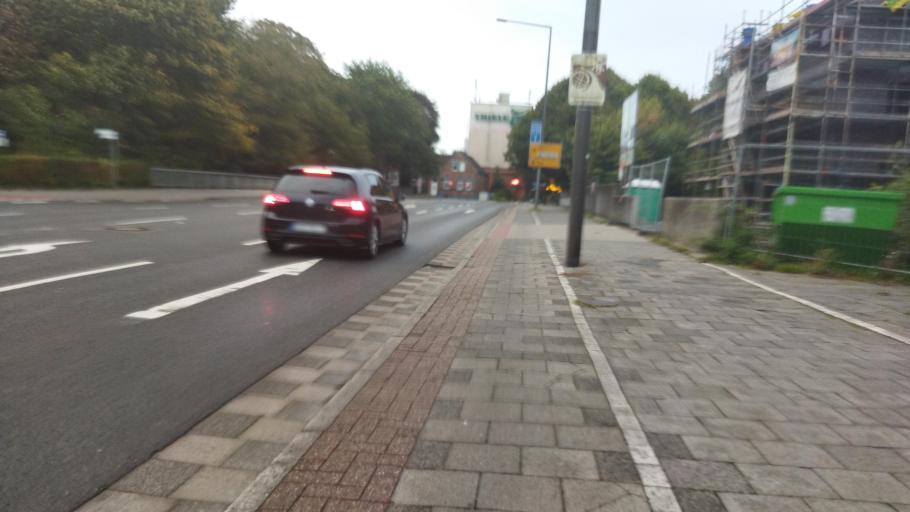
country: DE
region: Lower Saxony
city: Emden
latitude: 53.3746
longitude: 7.2072
